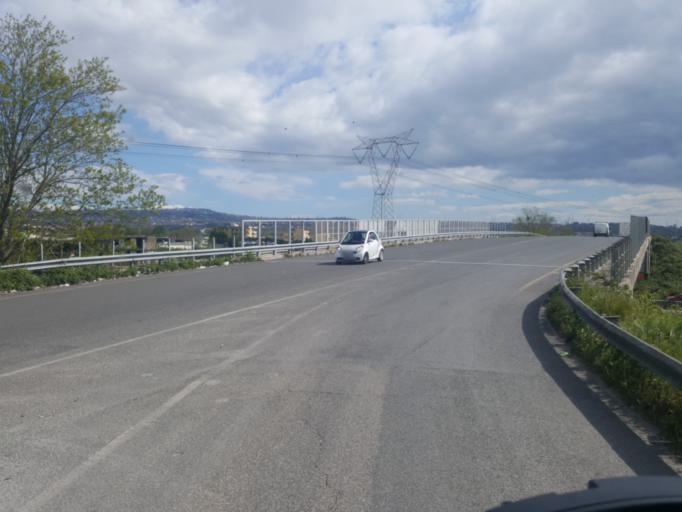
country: IT
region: Campania
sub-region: Provincia di Napoli
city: Torretta-Scalzapecora
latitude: 40.9312
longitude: 14.1224
